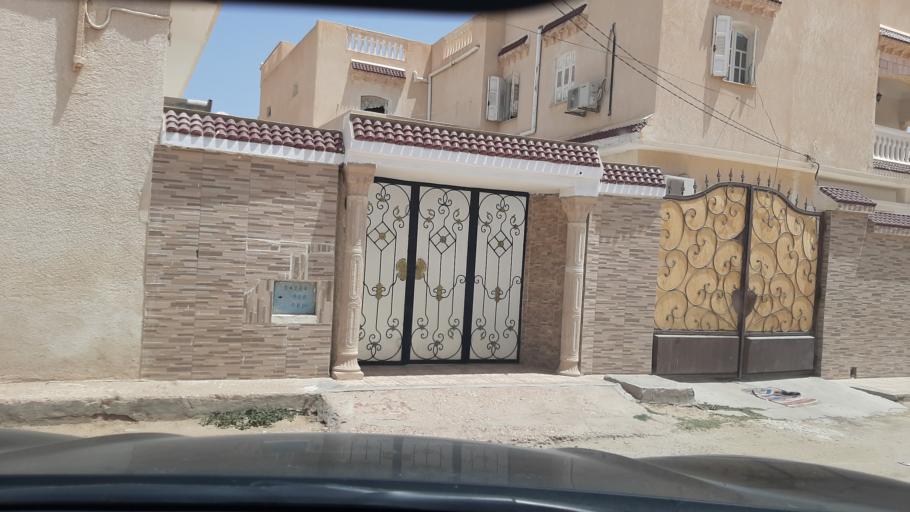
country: TN
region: Qabis
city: Matmata
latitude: 33.6175
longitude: 10.2800
